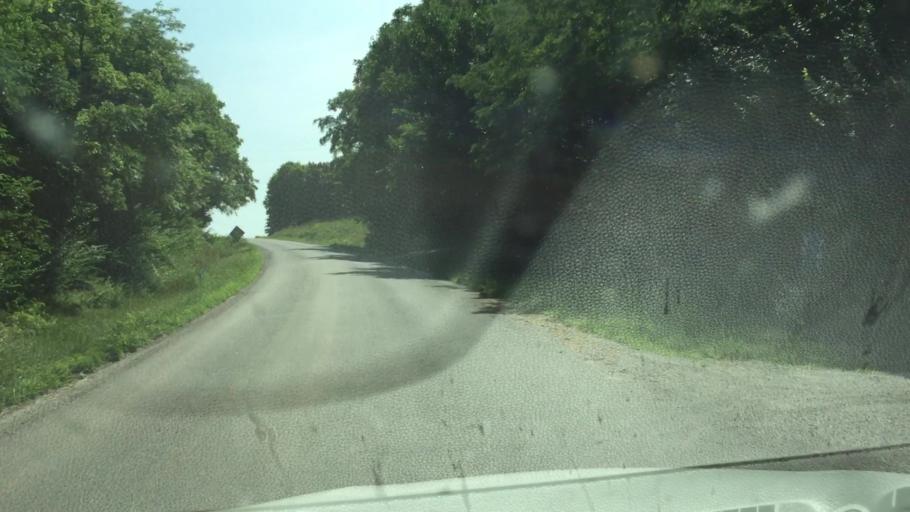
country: US
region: Illinois
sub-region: Hancock County
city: Nauvoo
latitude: 40.5119
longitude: -91.3579
